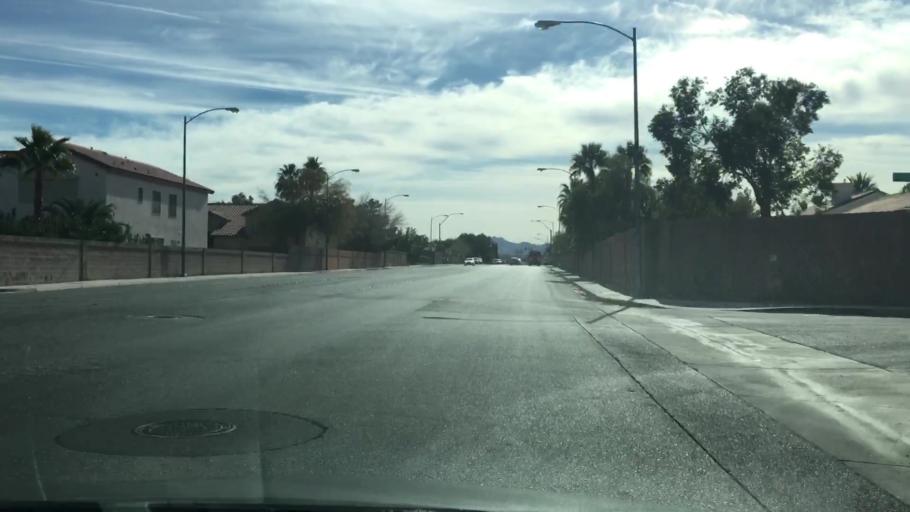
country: US
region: Nevada
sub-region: Clark County
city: Whitney
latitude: 36.0370
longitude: -115.1273
